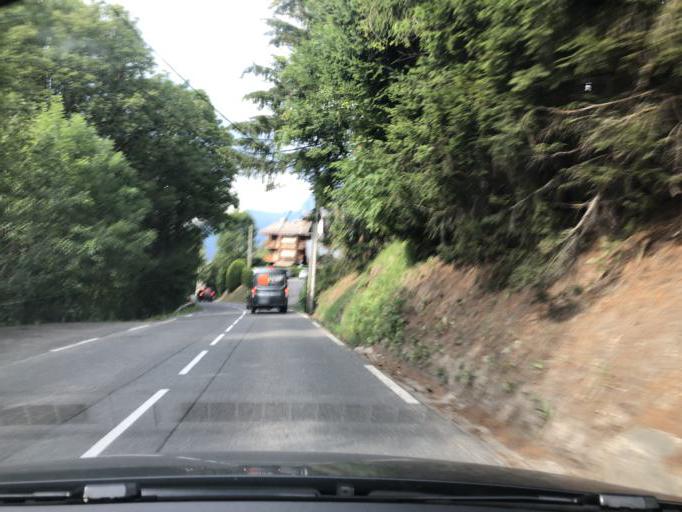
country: FR
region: Rhone-Alpes
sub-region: Departement de la Haute-Savoie
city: Megeve
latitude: 45.8615
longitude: 6.6309
